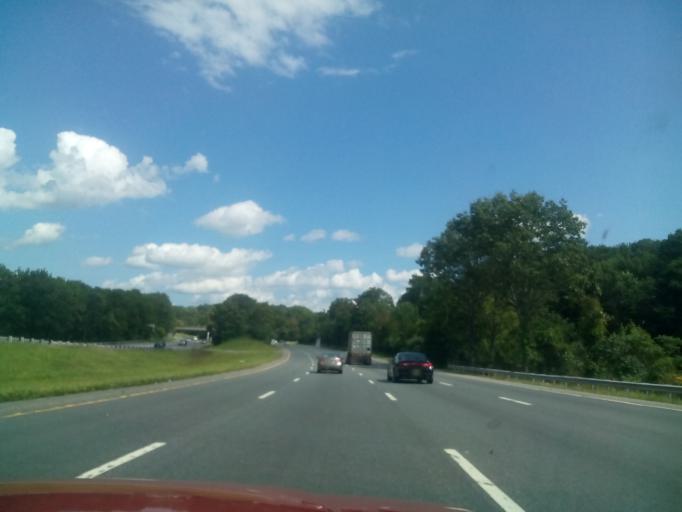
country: US
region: New Jersey
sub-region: Warren County
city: Belvidere
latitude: 40.9226
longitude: -75.0636
